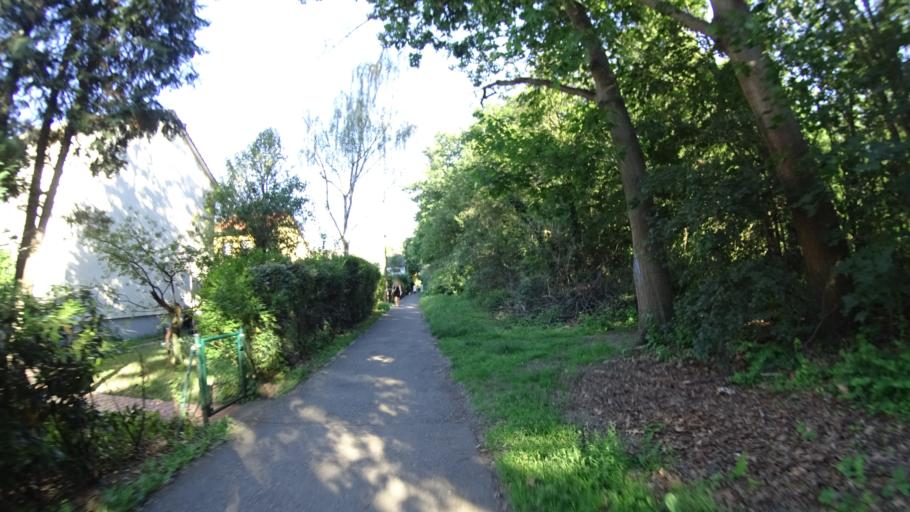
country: DE
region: Baden-Wuerttemberg
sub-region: Karlsruhe Region
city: Karlsruhe
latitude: 49.0227
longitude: 8.3716
